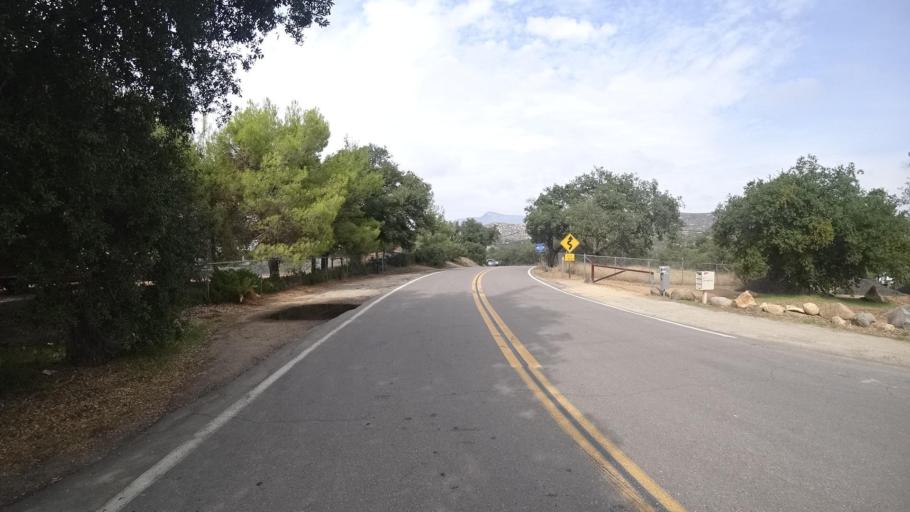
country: US
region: California
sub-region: San Diego County
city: Descanso
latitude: 32.8661
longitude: -116.6333
